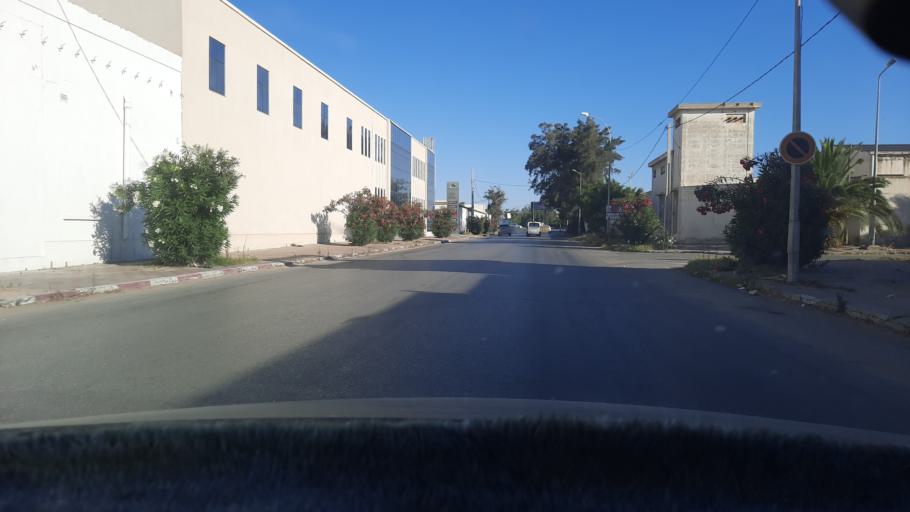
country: TN
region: Safaqis
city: Sfax
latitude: 34.7295
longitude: 10.7486
